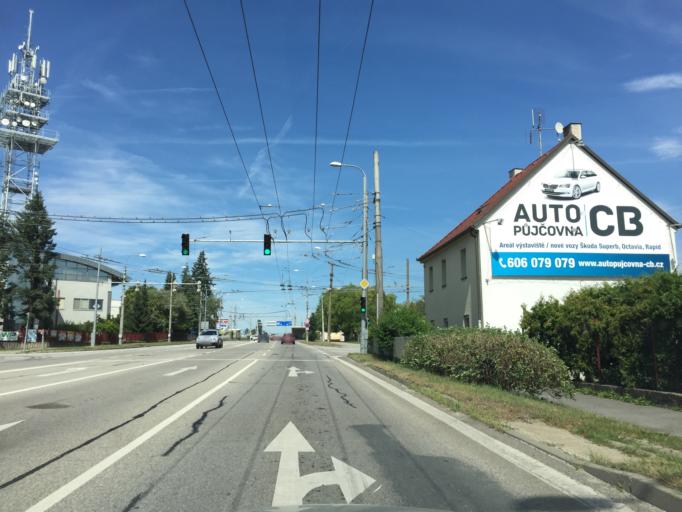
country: CZ
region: Jihocesky
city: Hrdejovice
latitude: 48.9982
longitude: 14.4812
